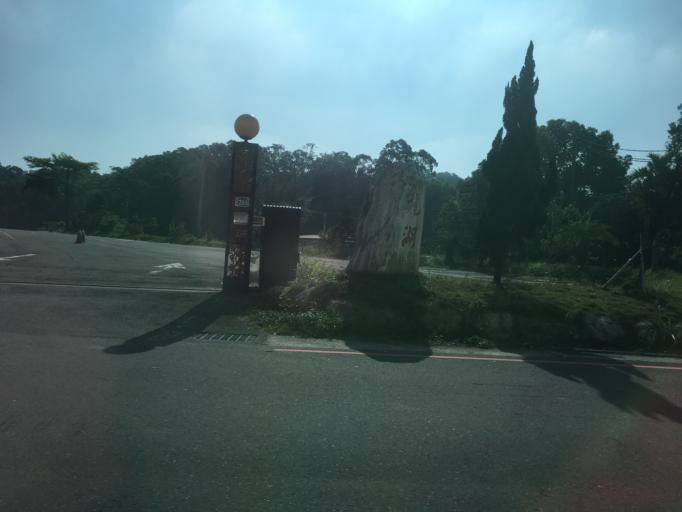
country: TW
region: Taiwan
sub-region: Hsinchu
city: Hsinchu
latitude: 24.7599
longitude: 120.9592
